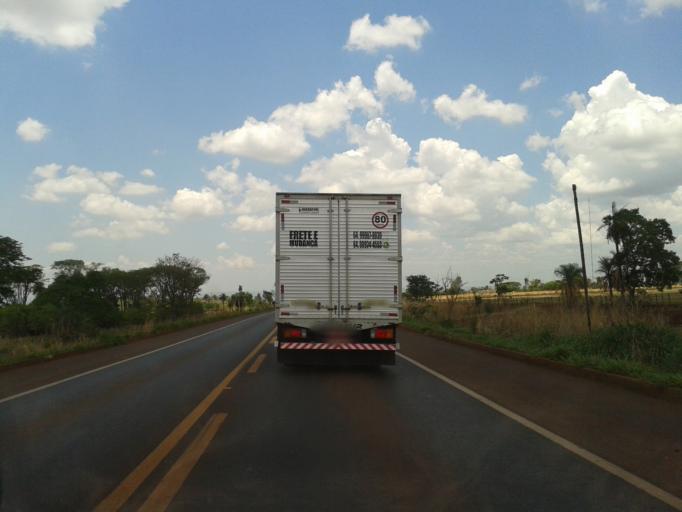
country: BR
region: Goias
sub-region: Itumbiara
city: Itumbiara
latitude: -18.3901
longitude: -49.3369
